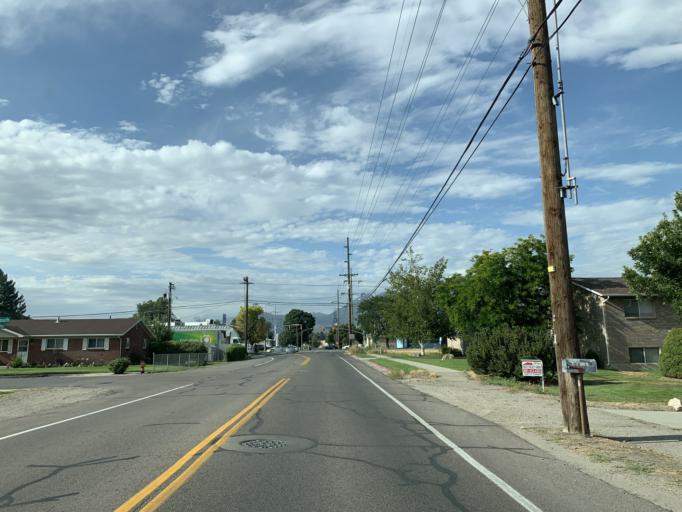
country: US
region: Utah
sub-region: Utah County
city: Provo
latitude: 40.2326
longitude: -111.6874
